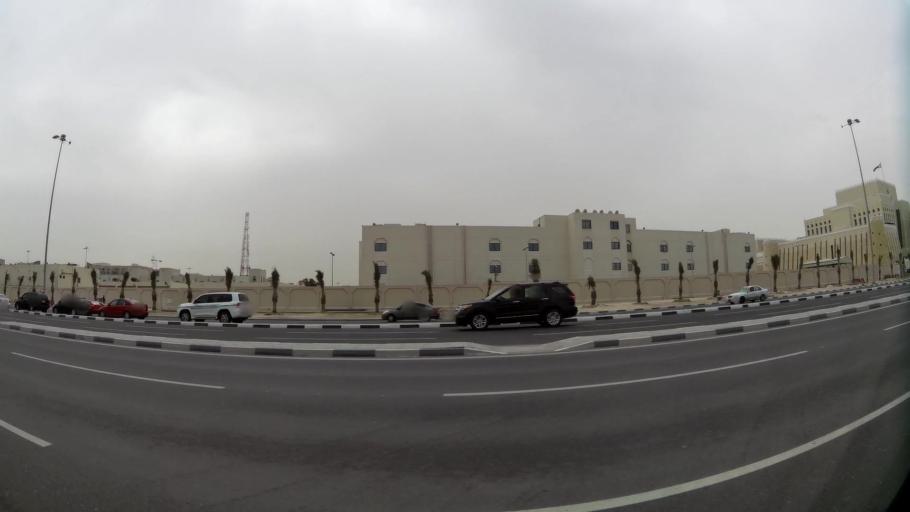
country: QA
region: Baladiyat ad Dawhah
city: Doha
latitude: 25.3036
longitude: 51.5067
